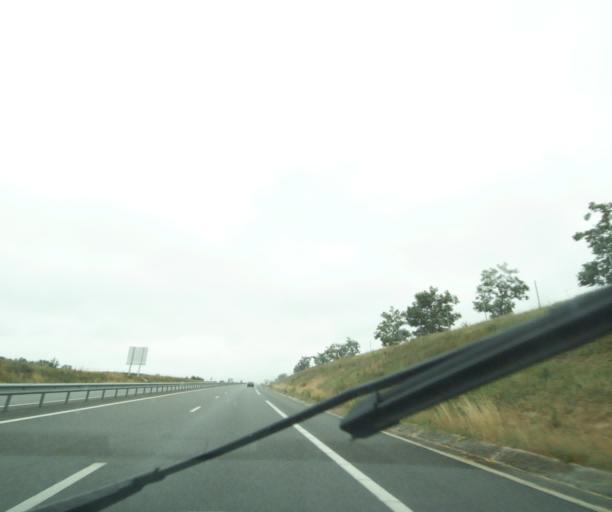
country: FR
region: Midi-Pyrenees
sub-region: Departement du Tarn
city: Le Garric
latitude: 44.0216
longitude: 2.1840
